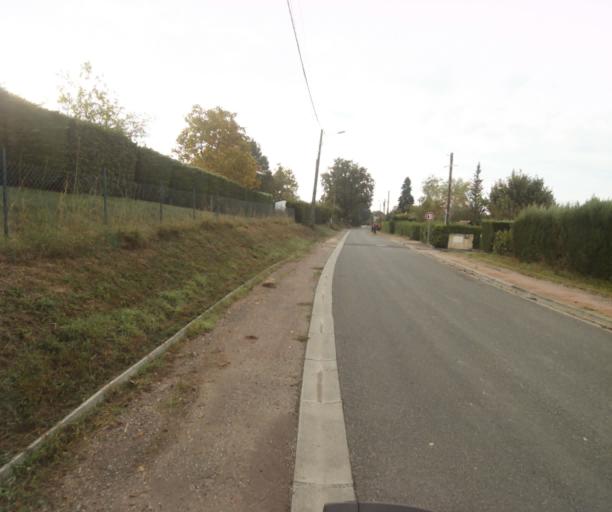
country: FR
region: Midi-Pyrenees
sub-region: Departement du Tarn-et-Garonne
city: Montech
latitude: 43.9656
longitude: 1.2258
